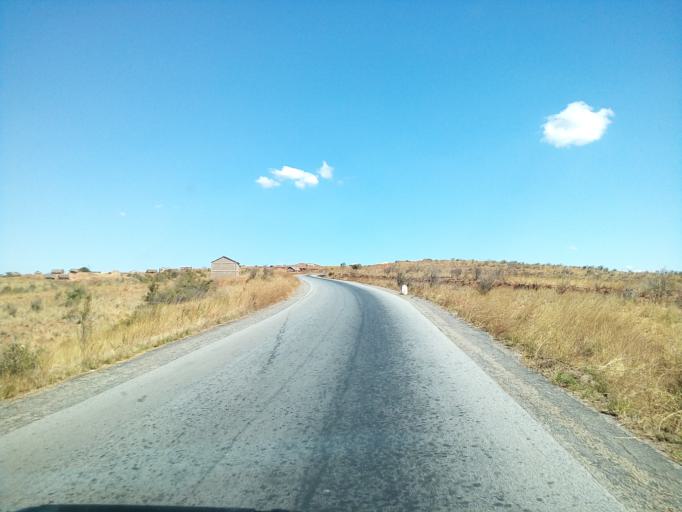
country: MG
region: Betsiboka
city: Maevatanana
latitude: -17.4161
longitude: 46.9187
